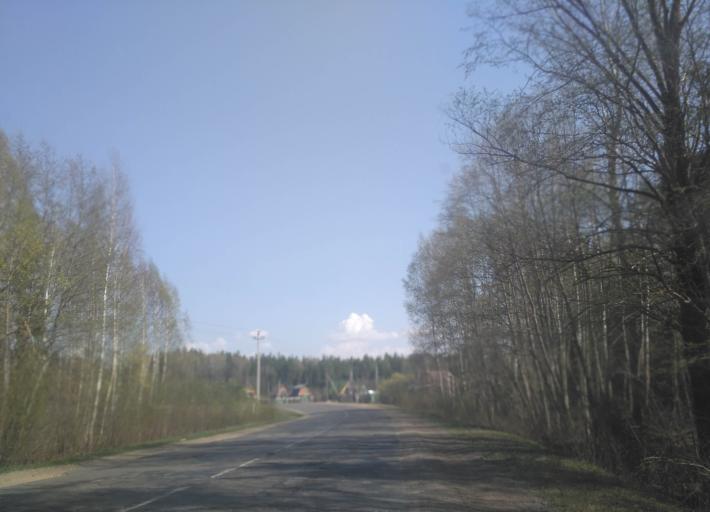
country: BY
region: Minsk
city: Loshnitsa
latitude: 54.4204
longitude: 28.6455
